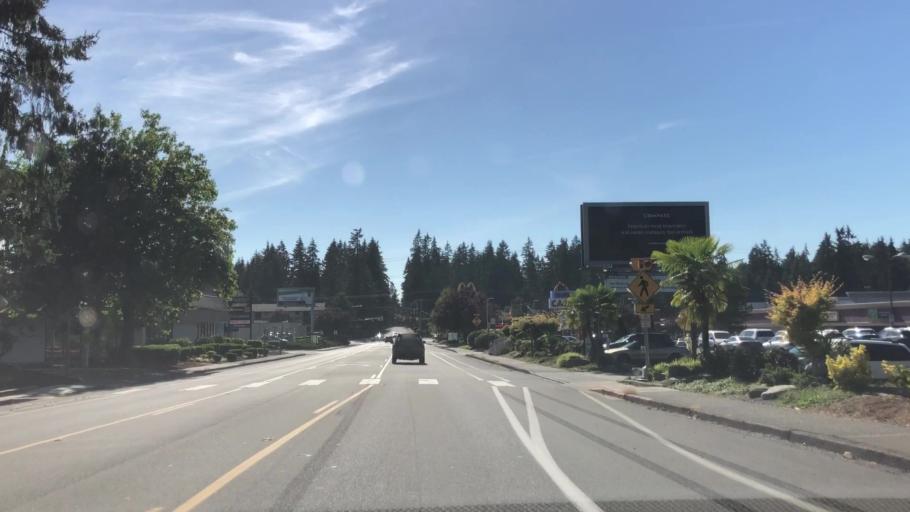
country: US
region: Washington
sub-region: King County
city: Kingsgate
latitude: 47.7313
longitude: -122.1725
